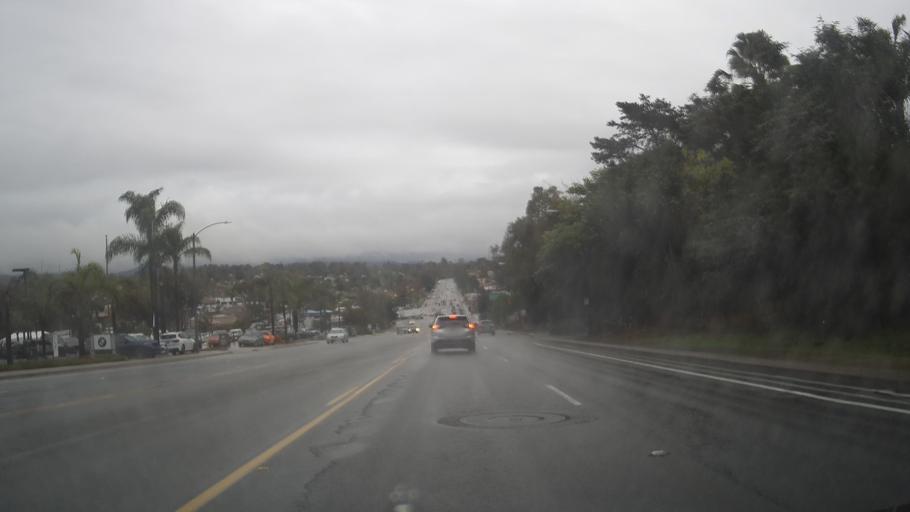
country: US
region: California
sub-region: San Diego County
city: Encinitas
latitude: 33.0461
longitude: -117.2635
